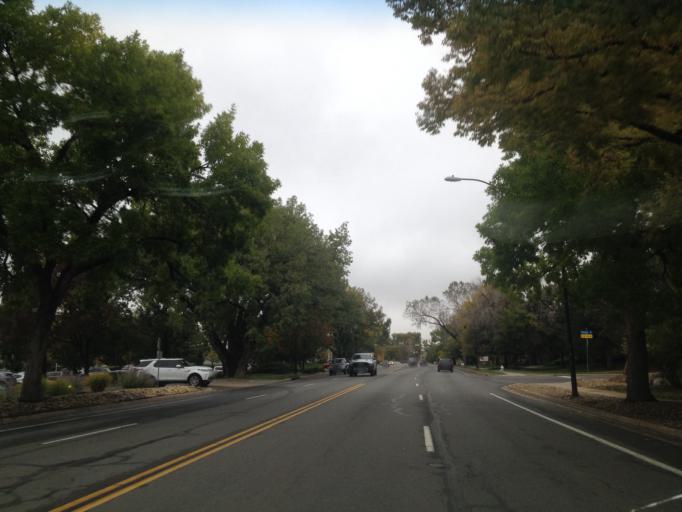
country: US
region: Colorado
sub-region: Boulder County
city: Boulder
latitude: 40.0345
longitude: -105.2537
